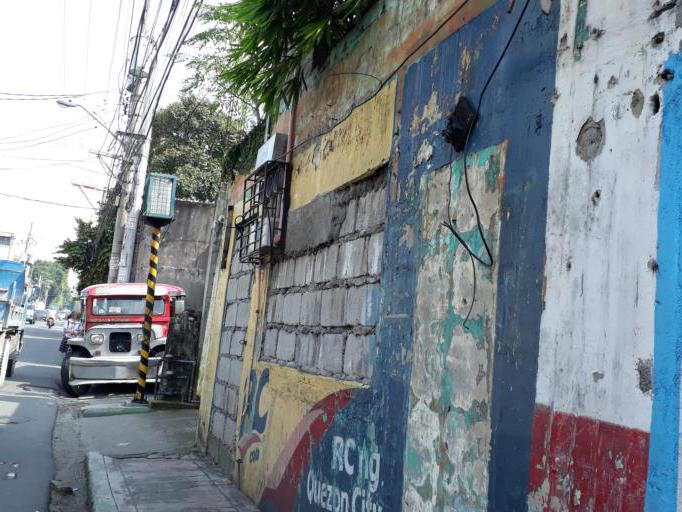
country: PH
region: Calabarzon
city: Bagong Pagasa
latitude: 14.6673
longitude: 121.0073
